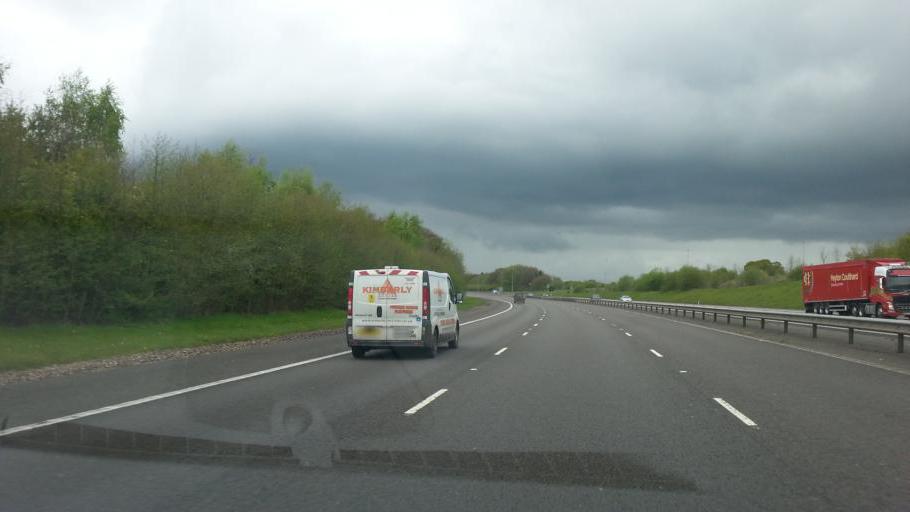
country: GB
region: England
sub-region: City and Borough of Birmingham
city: Sutton Coldfield
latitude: 52.5774
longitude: -1.7777
